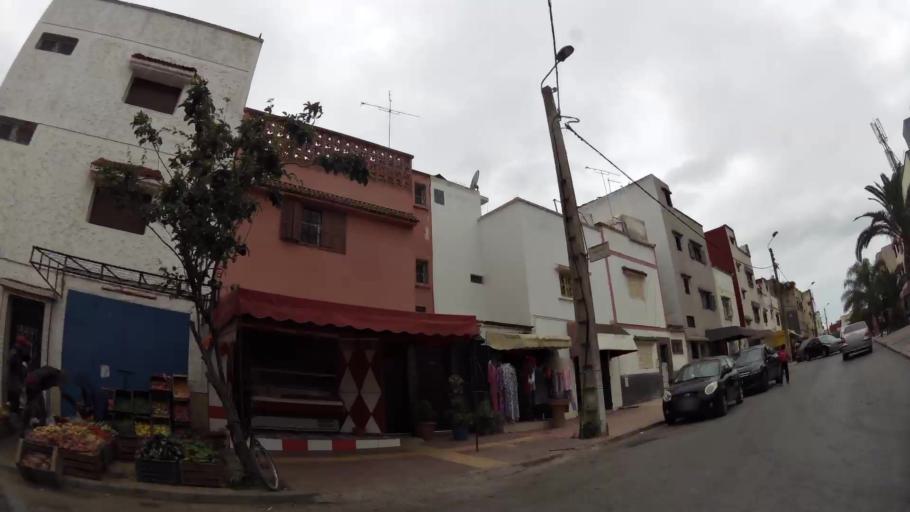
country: MA
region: Rabat-Sale-Zemmour-Zaer
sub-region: Rabat
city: Rabat
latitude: 33.9719
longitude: -6.8187
